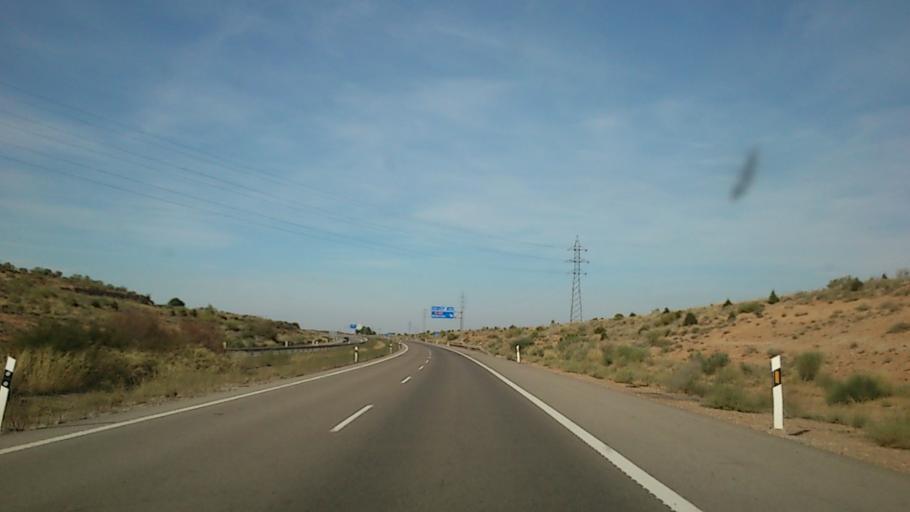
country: ES
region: Aragon
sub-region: Provincia de Zaragoza
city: Botorrita
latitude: 41.5078
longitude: -1.0450
